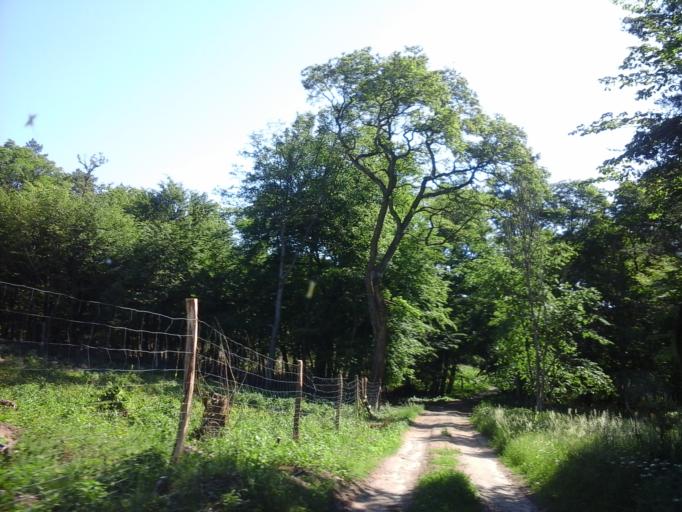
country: PL
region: West Pomeranian Voivodeship
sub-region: Powiat choszczenski
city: Recz
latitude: 53.1941
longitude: 15.5137
